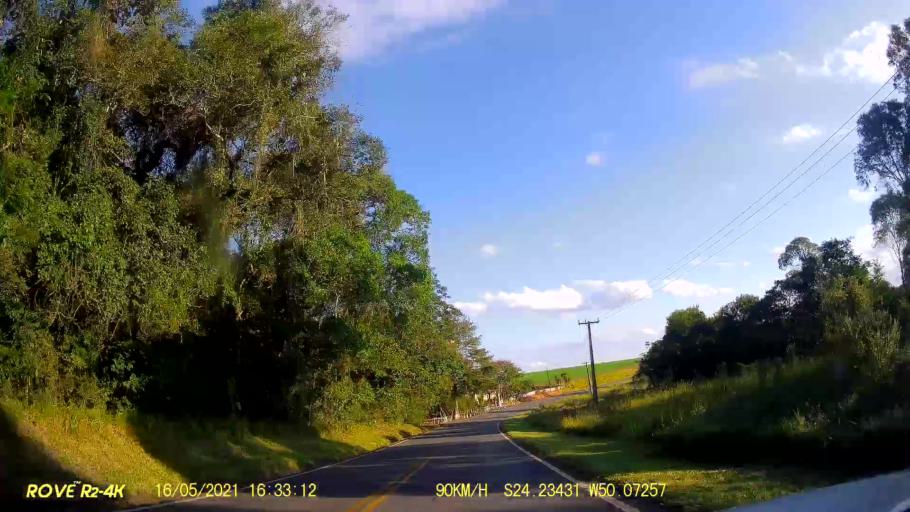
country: BR
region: Parana
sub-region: Pirai Do Sul
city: Pirai do Sul
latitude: -24.2344
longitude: -50.0726
